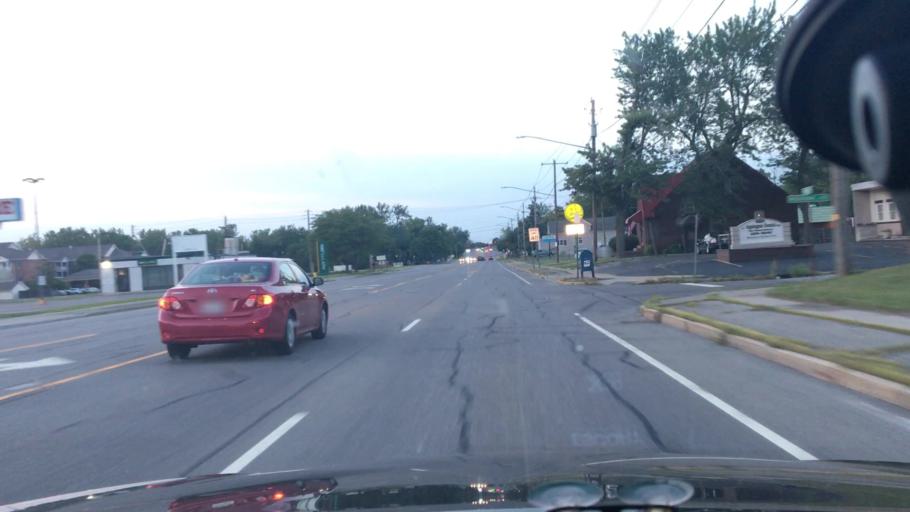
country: US
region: New York
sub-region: Erie County
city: Cheektowaga
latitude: 42.8591
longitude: -78.7545
